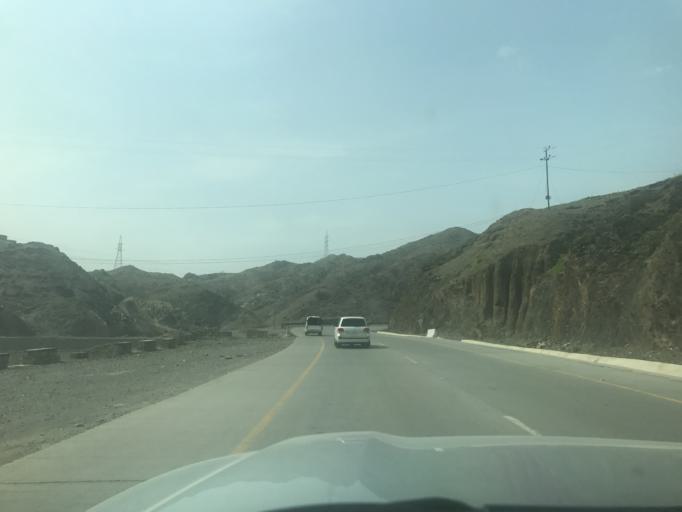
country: PK
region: Federally Administered Tribal Areas
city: Landi Kotal
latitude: 34.0052
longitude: 71.3108
